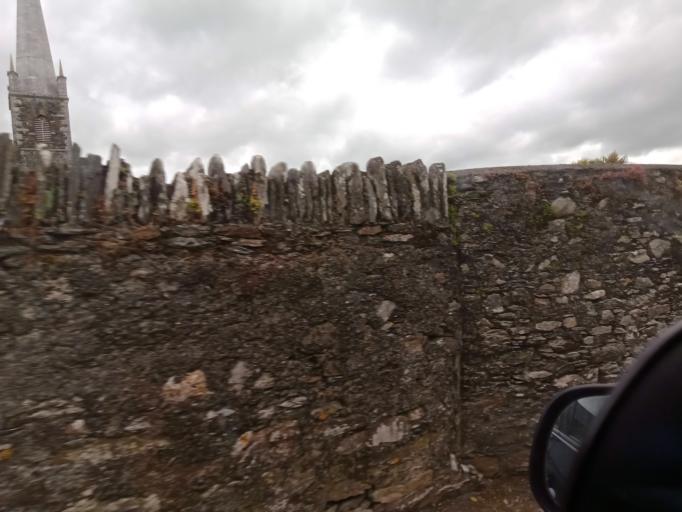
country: IE
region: Munster
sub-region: County Cork
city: Derry
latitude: 51.5775
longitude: -9.0296
